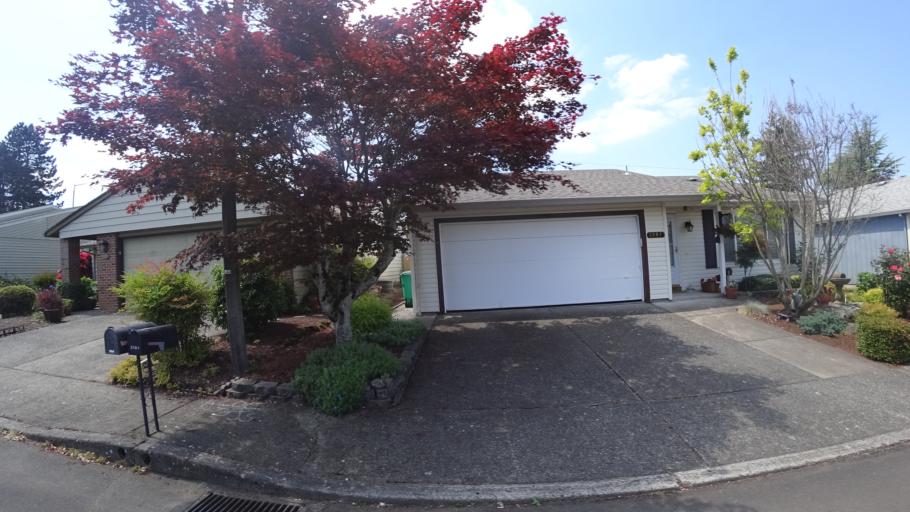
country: US
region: Oregon
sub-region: Multnomah County
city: Fairview
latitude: 45.5378
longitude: -122.5098
